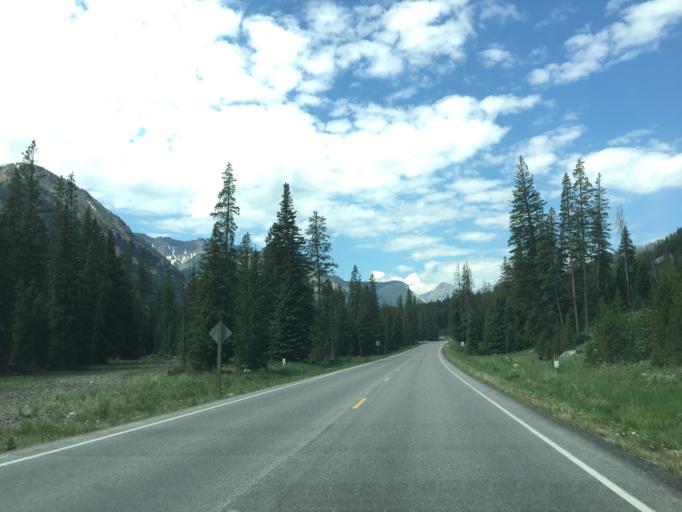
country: US
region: Montana
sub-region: Stillwater County
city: Absarokee
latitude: 45.0175
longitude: -109.9641
